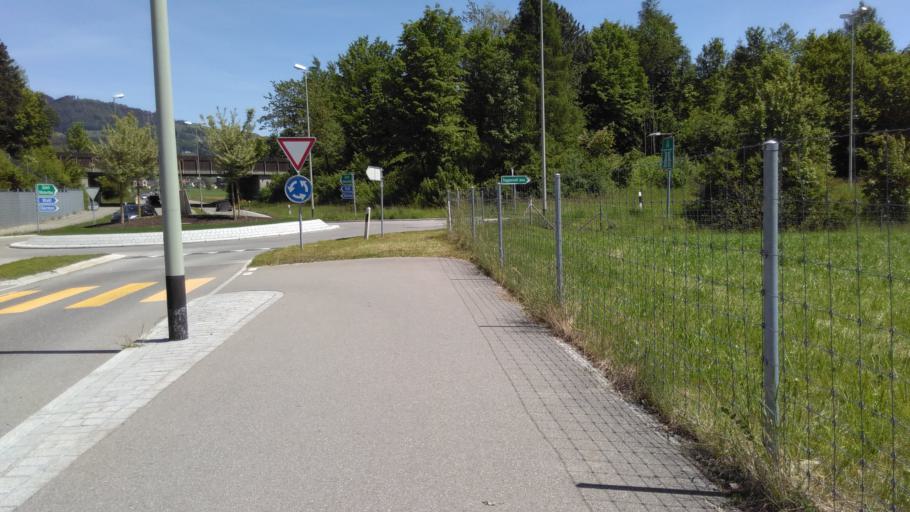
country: CH
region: Zurich
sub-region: Bezirk Hinwil
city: Bubikon
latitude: 47.2738
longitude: 8.8285
